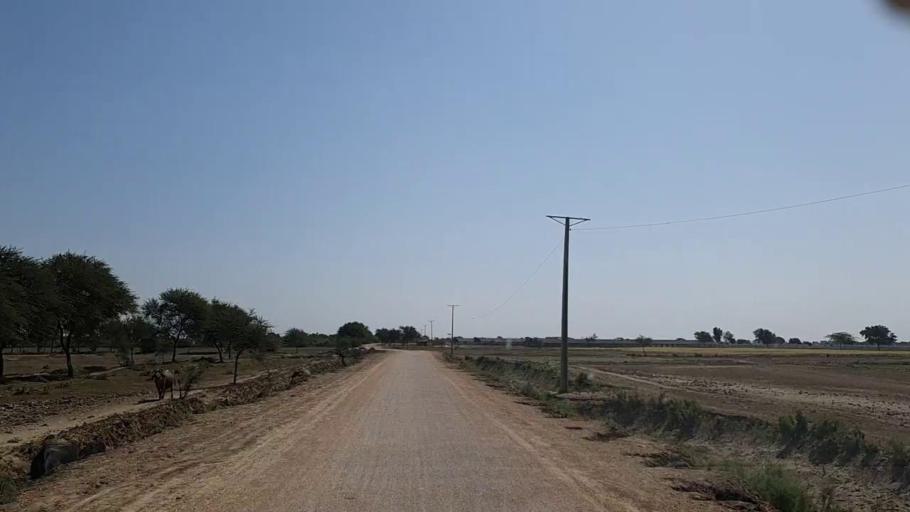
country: PK
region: Sindh
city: Mirpur Batoro
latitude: 24.6799
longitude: 68.2978
